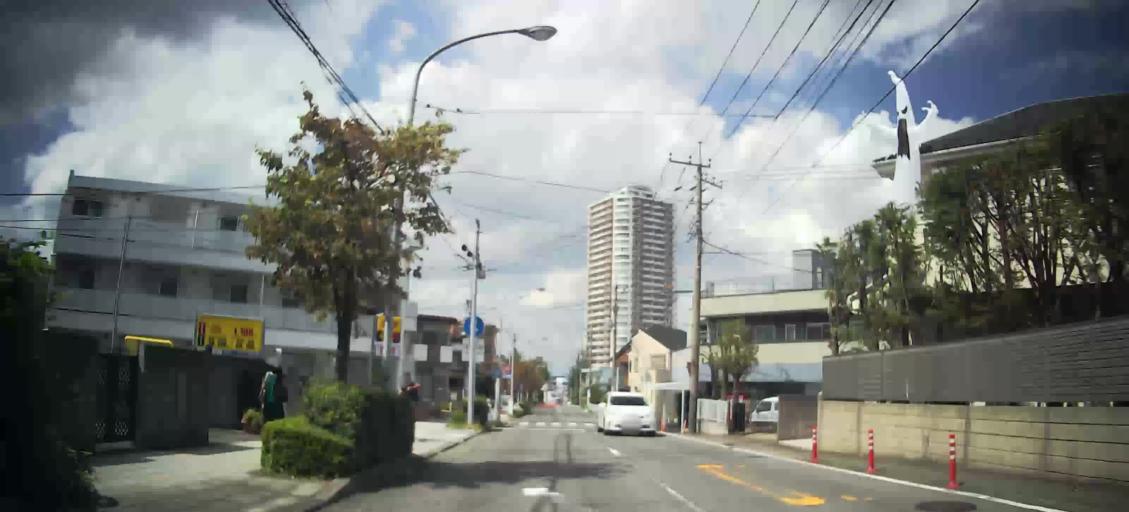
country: JP
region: Kanagawa
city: Yokohama
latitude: 35.4727
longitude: 139.5518
